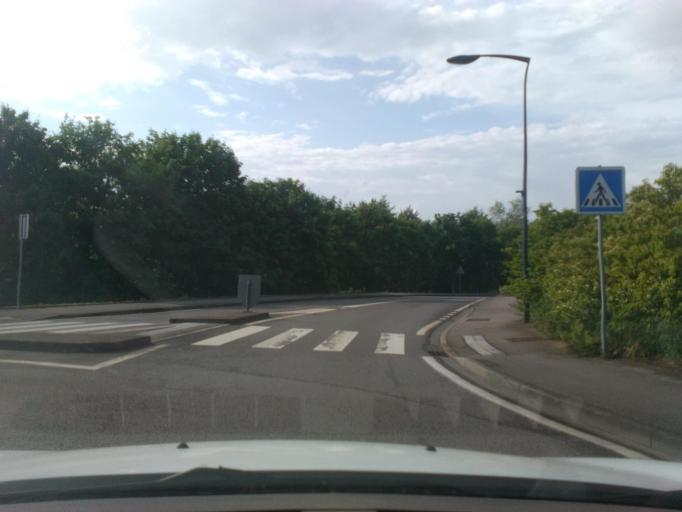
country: FR
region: Lorraine
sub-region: Departement de Meurthe-et-Moselle
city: Frouard
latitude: 48.7753
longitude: 6.1347
